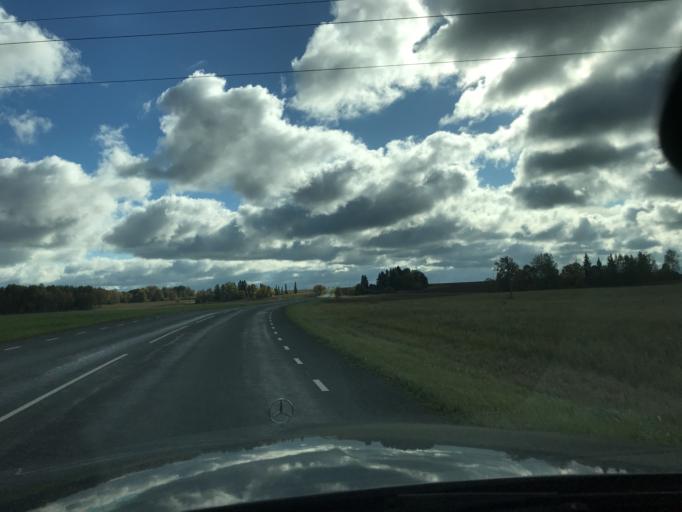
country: EE
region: Vorumaa
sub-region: Antsla vald
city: Vana-Antsla
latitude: 57.9249
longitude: 26.3396
